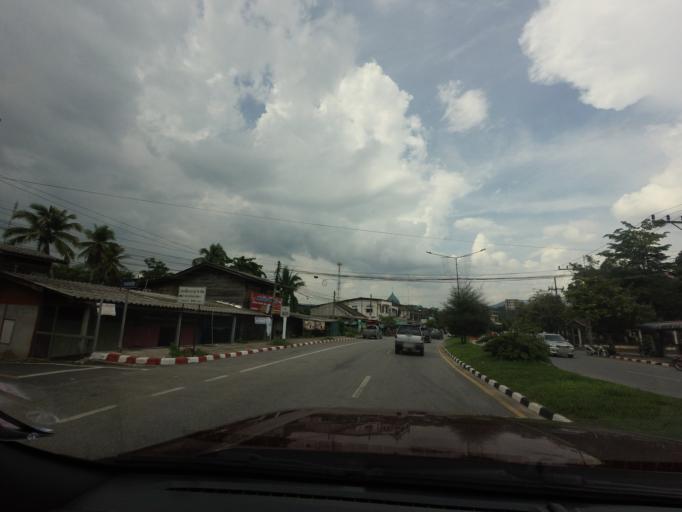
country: TH
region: Yala
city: Ban Nang Sata
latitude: 6.2667
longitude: 101.2636
